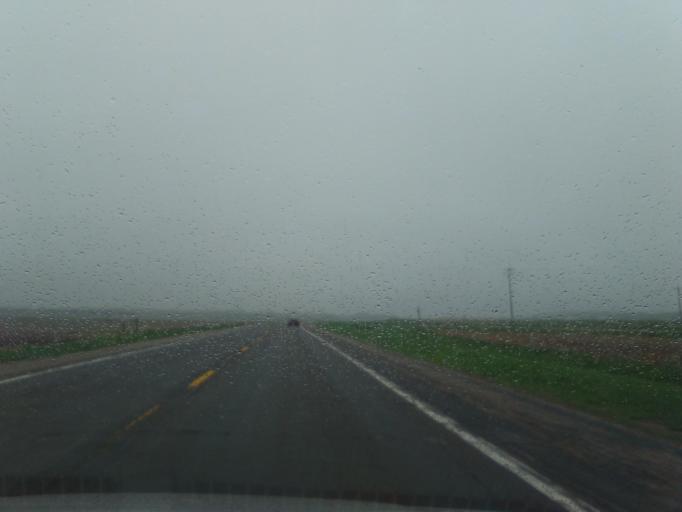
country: US
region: Nebraska
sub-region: Cuming County
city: Wisner
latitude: 41.9594
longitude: -96.8735
